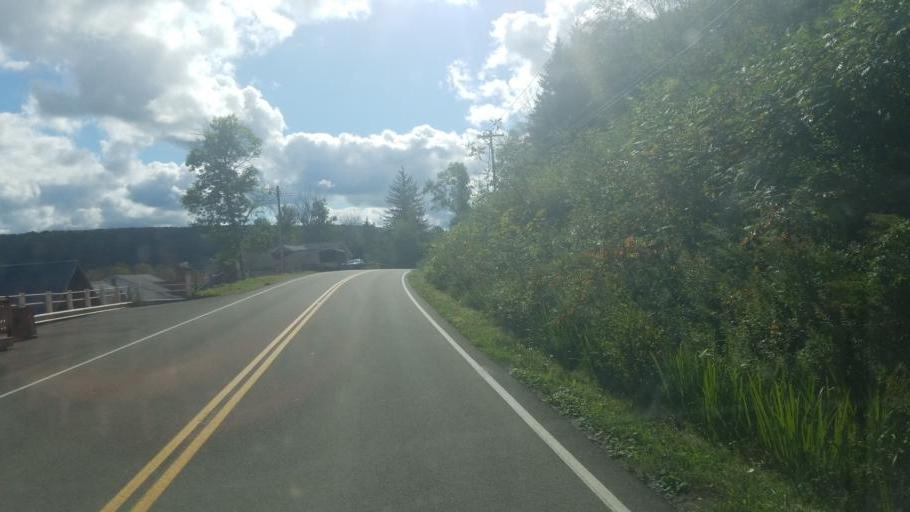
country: US
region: New York
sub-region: Allegany County
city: Cuba
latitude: 42.2456
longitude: -78.2791
